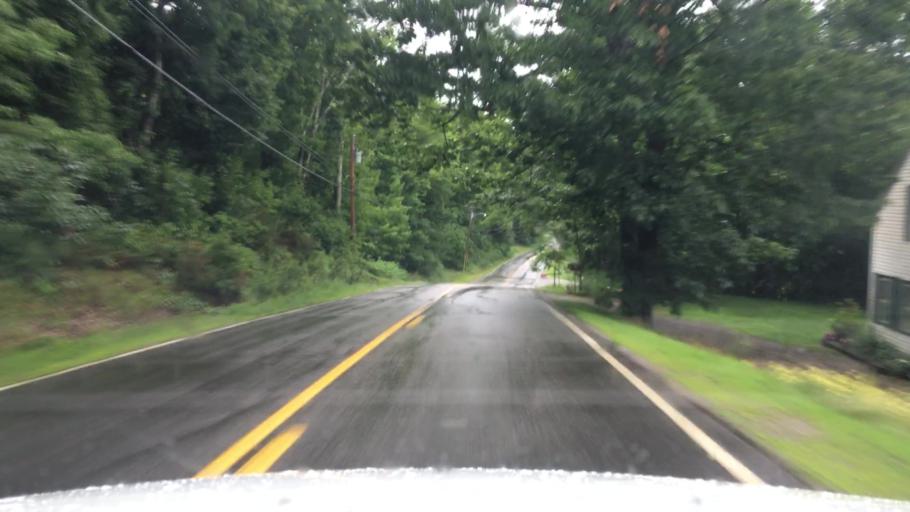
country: US
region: Maine
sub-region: Kennebec County
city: Winthrop
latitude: 44.2992
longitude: -69.9259
